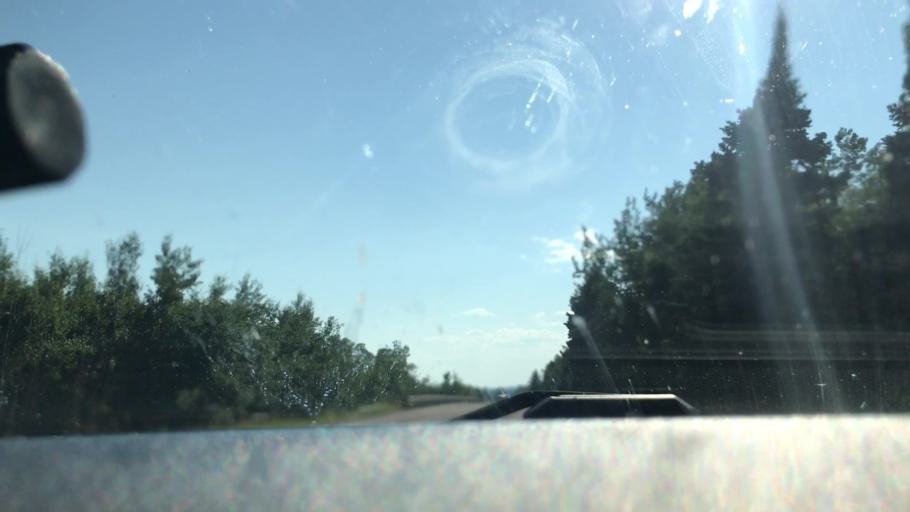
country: US
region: Minnesota
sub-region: Cook County
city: Grand Marais
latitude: 47.8233
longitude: -90.0283
